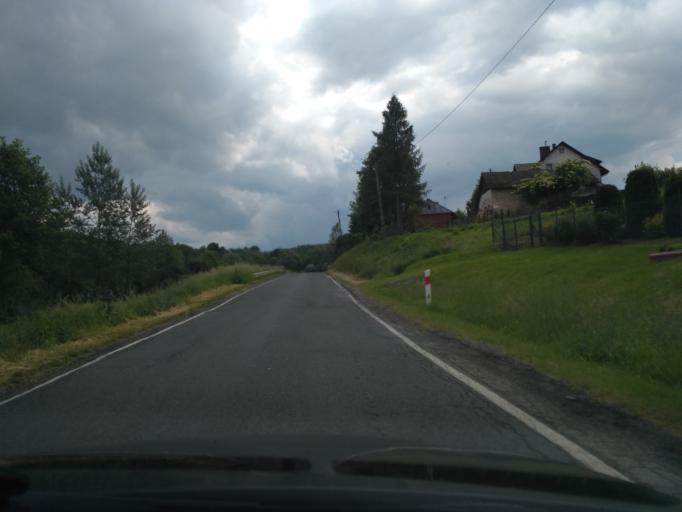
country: PL
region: Subcarpathian Voivodeship
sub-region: Powiat przeworski
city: Jawornik Polski
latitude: 49.9073
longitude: 22.3063
